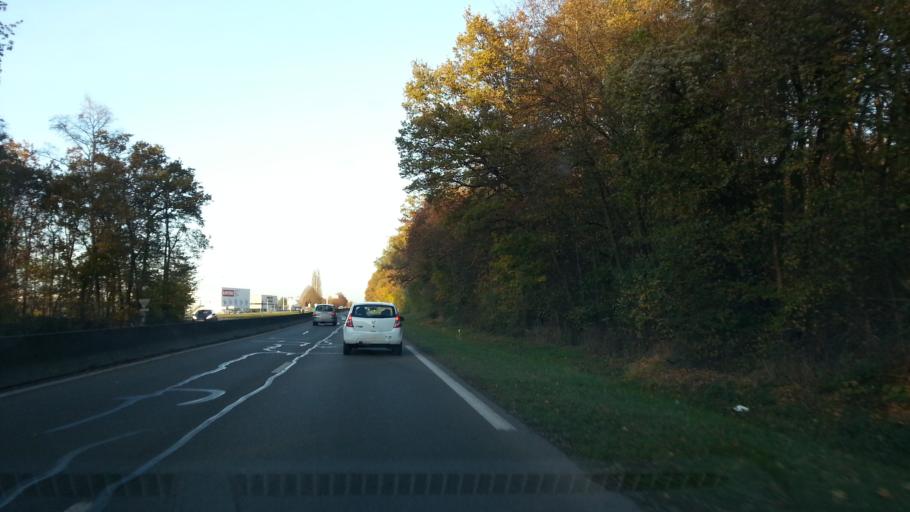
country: FR
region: Picardie
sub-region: Departement de l'Oise
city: Saint-Maximin
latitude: 49.2272
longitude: 2.4692
